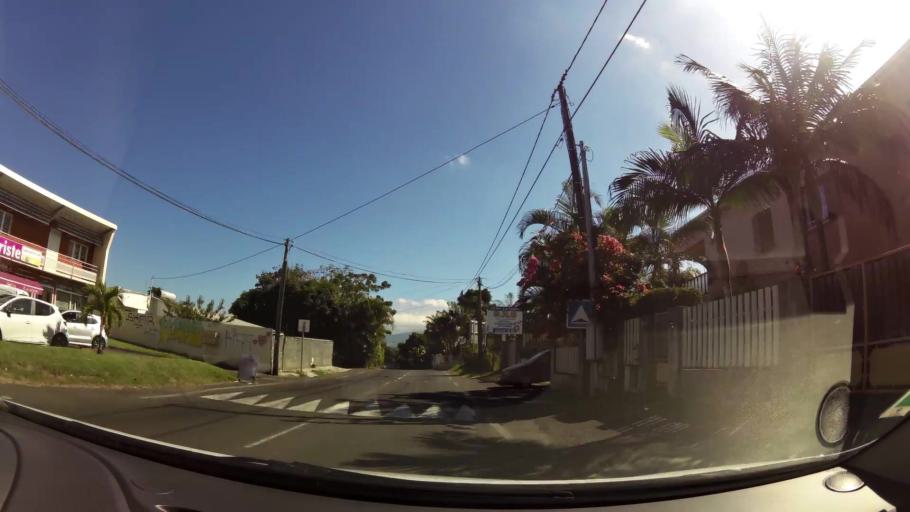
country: RE
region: Reunion
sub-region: Reunion
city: Le Tampon
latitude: -21.2854
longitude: 55.5074
